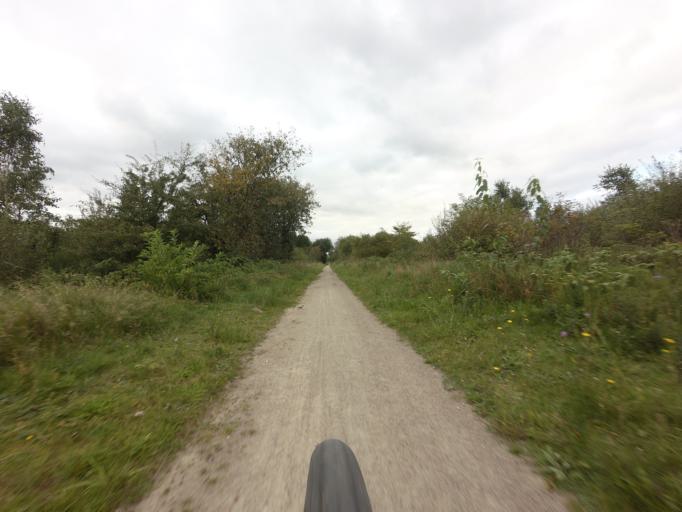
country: DK
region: South Denmark
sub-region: Billund Kommune
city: Billund
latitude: 55.8223
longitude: 9.0315
